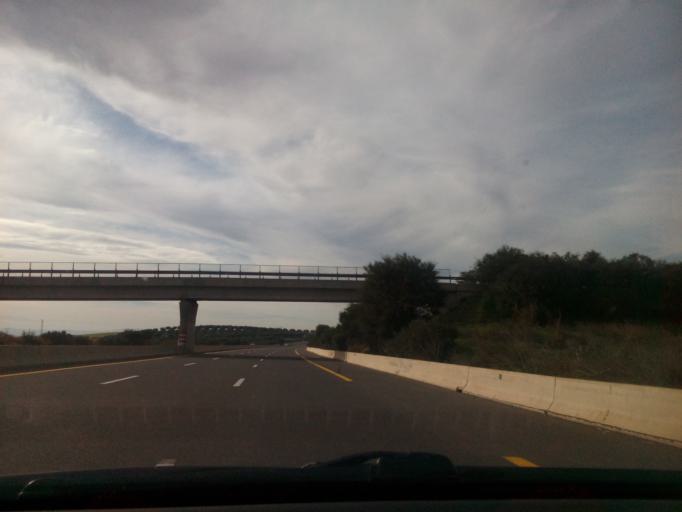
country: DZ
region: Sidi Bel Abbes
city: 'Ain el Berd
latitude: 35.3417
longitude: -0.5173
